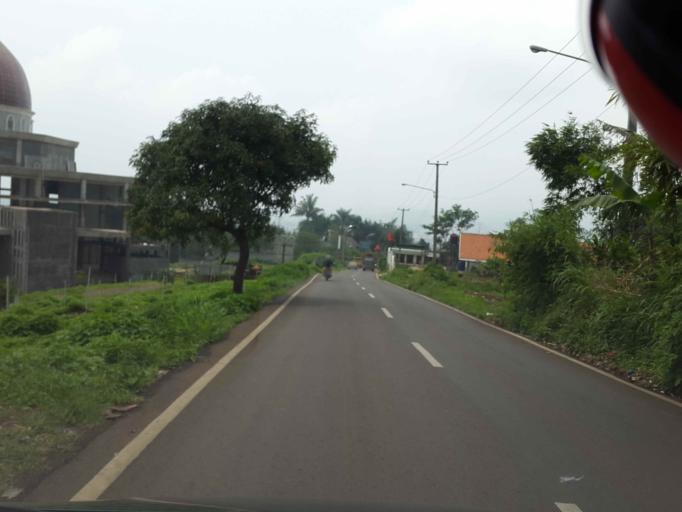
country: ID
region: West Java
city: Padalarang
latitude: -6.8387
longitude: 107.5109
